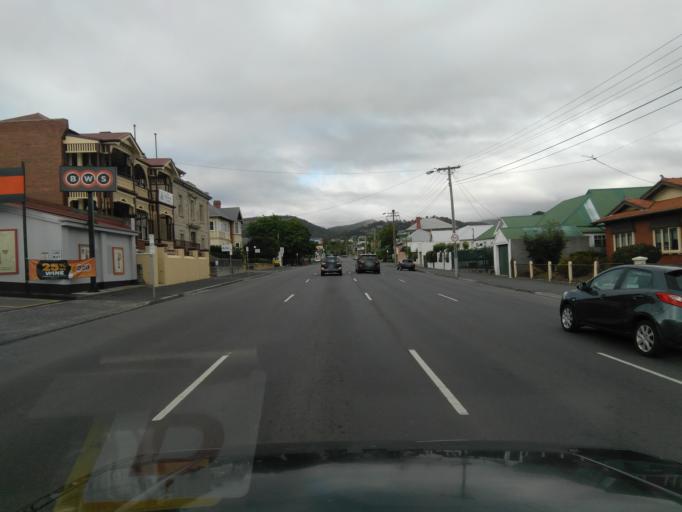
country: AU
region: Tasmania
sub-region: Hobart
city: Sandy Bay
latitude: -42.8896
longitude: 147.3231
